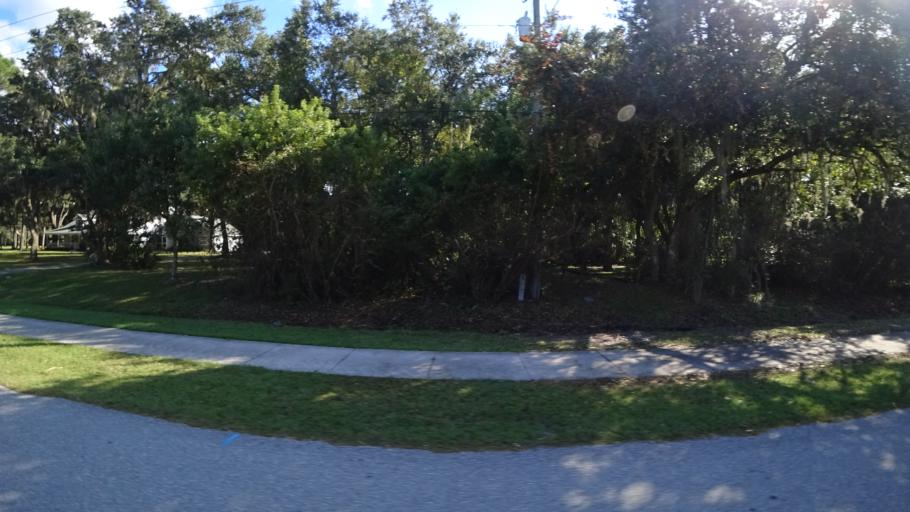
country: US
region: Florida
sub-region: Manatee County
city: Samoset
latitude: 27.4708
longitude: -82.4795
